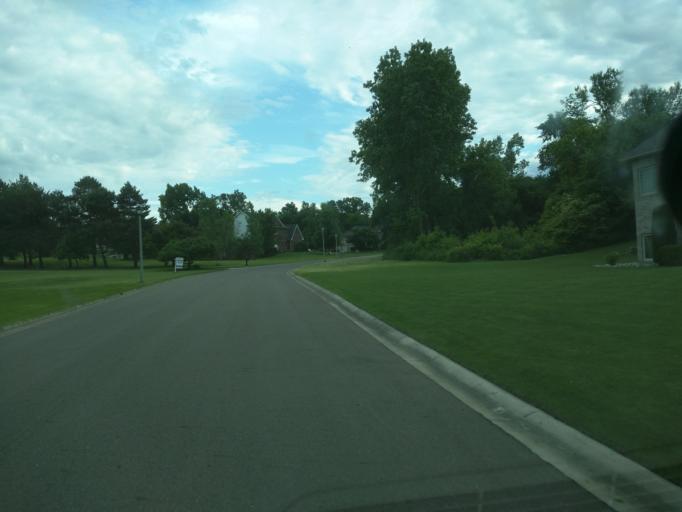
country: US
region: Michigan
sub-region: Eaton County
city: Waverly
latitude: 42.7543
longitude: -84.6150
